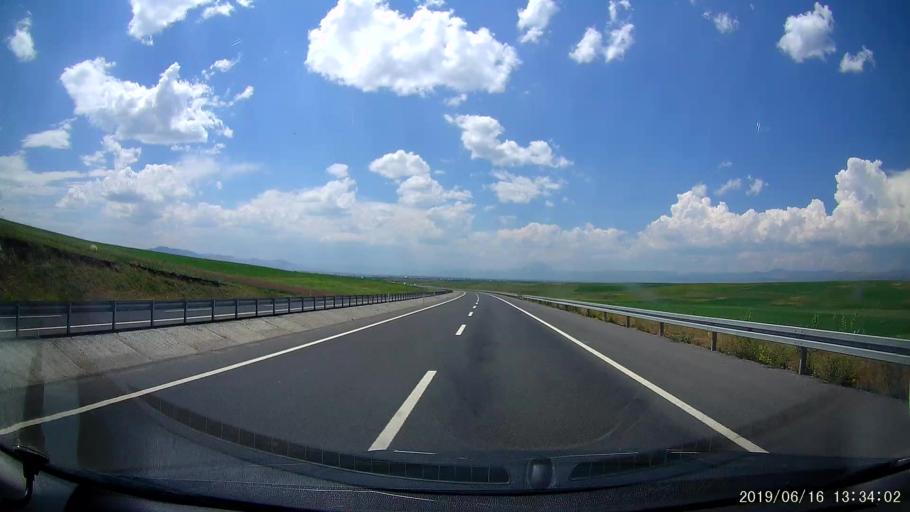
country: TR
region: Agri
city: Agri
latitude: 39.7107
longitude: 43.1381
